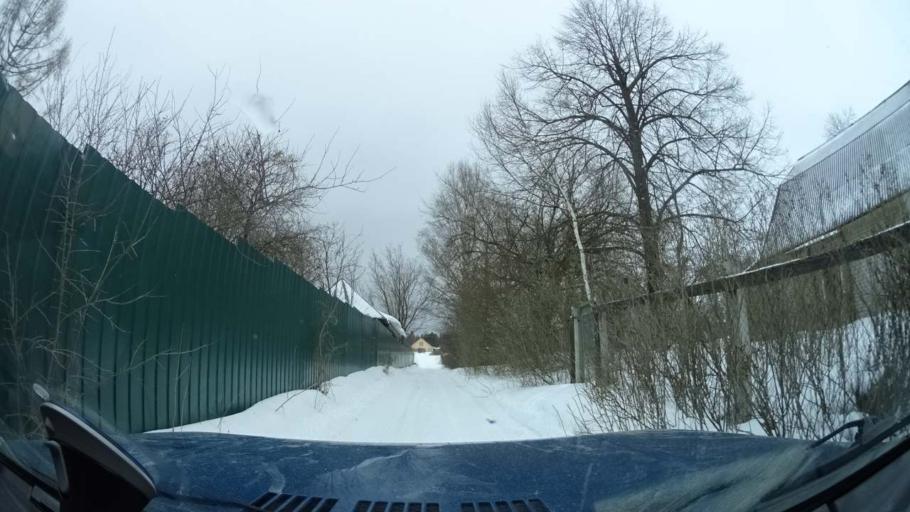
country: RU
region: Tverskaya
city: Radchenko
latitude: 56.6701
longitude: 36.4656
